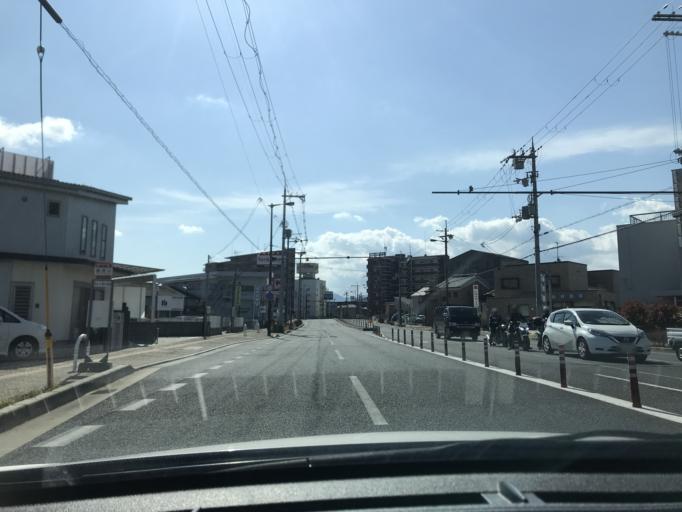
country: JP
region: Nara
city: Nara-shi
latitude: 34.6794
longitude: 135.8123
